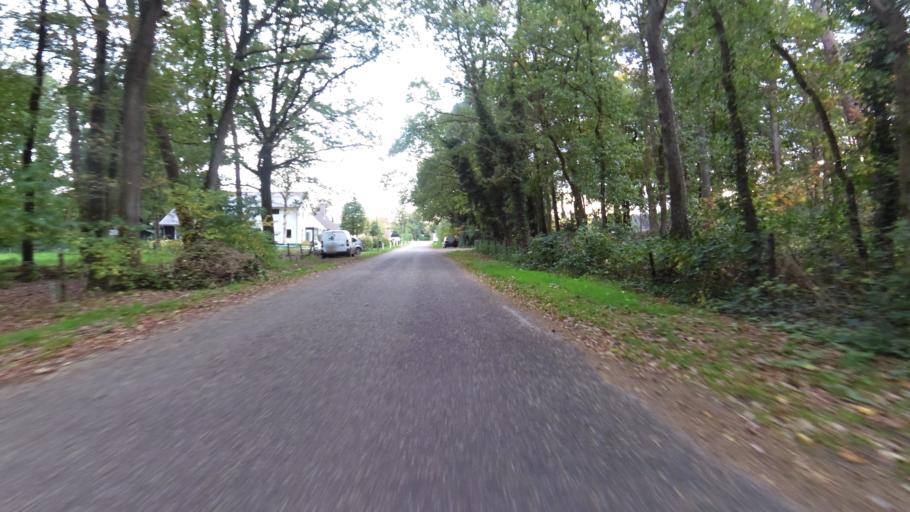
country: NL
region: Gelderland
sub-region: Gemeente Oldebroek
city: Oldebroek
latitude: 52.4426
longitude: 5.9488
